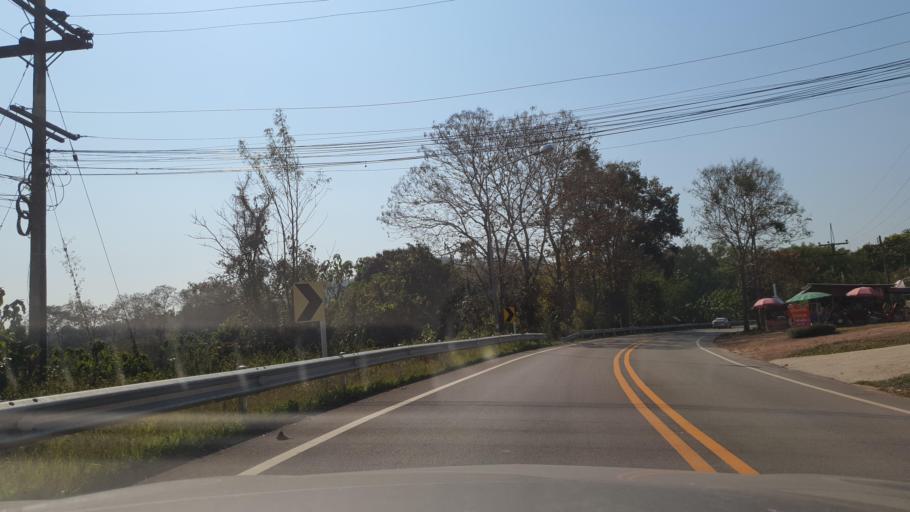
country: TH
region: Chiang Rai
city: Mae Lao
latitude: 19.8323
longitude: 99.6885
